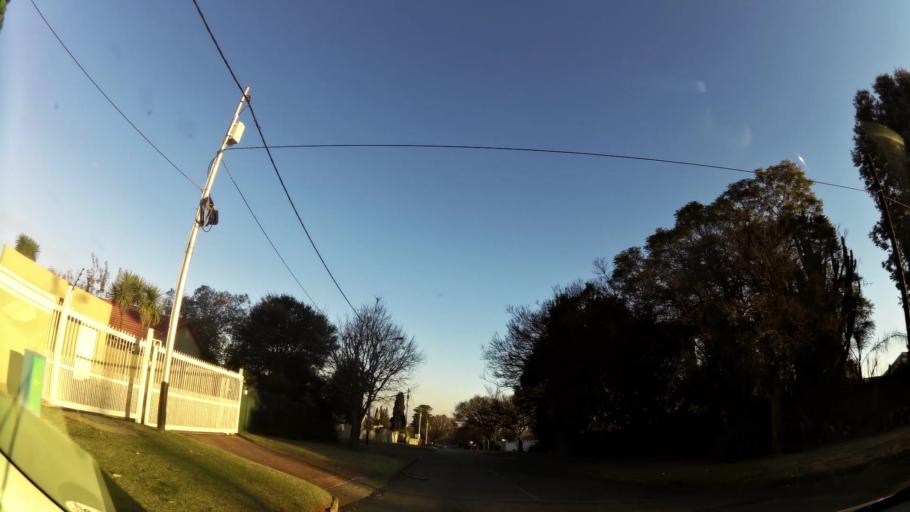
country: ZA
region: Gauteng
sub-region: City of Johannesburg Metropolitan Municipality
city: Roodepoort
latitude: -26.1514
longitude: 27.8846
